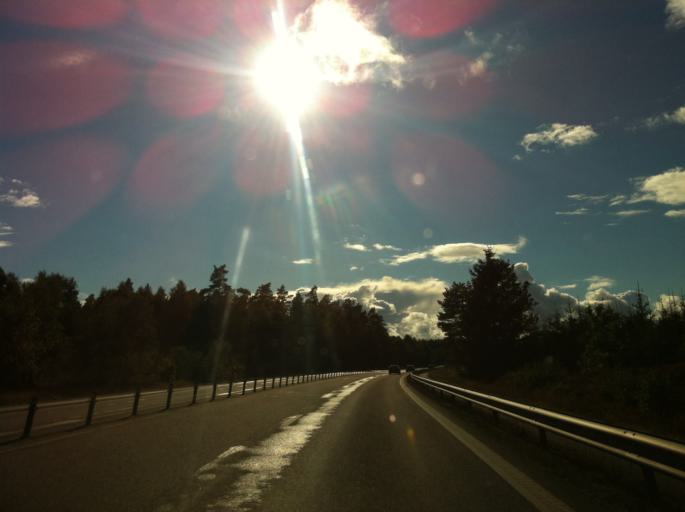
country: SE
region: Skane
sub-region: Hassleholms Kommun
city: Sosdala
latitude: 56.1585
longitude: 13.5651
